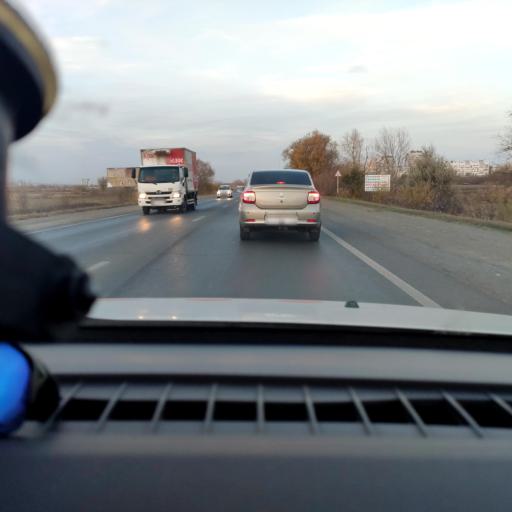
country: RU
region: Samara
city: Samara
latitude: 53.0890
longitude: 50.1472
